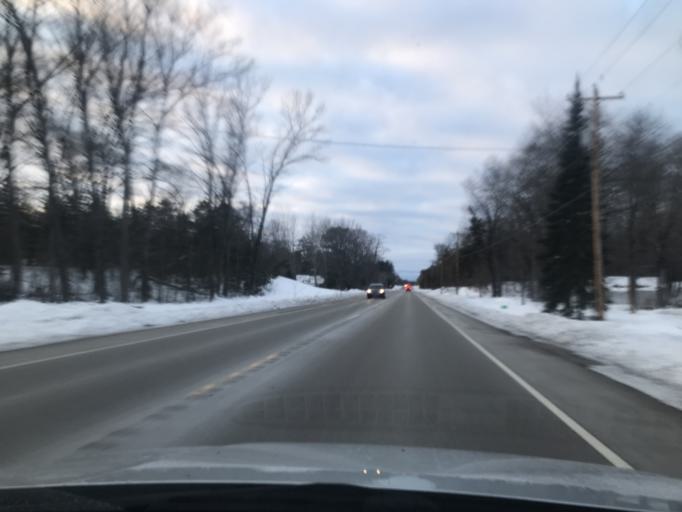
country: US
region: Wisconsin
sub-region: Marinette County
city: Marinette
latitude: 45.1552
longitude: -87.7114
